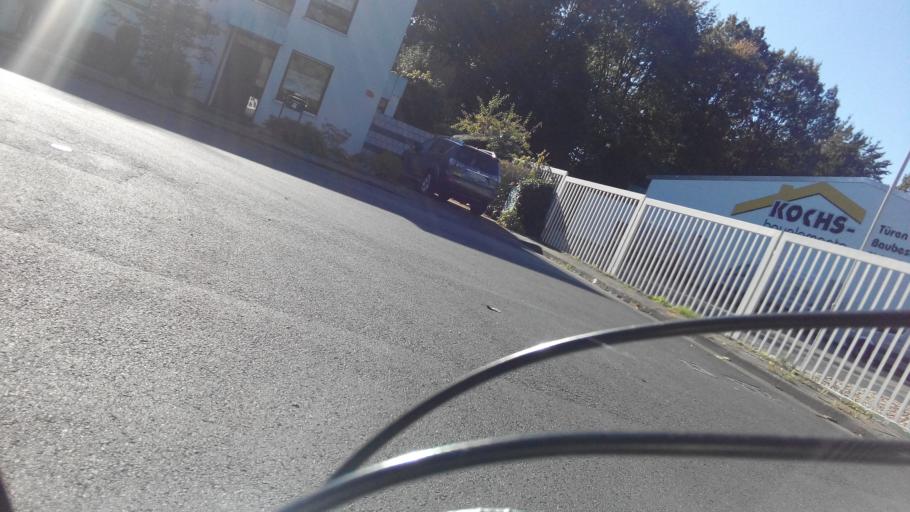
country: DE
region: North Rhine-Westphalia
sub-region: Regierungsbezirk Munster
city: Gelsenkirchen
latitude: 51.5023
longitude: 7.1297
